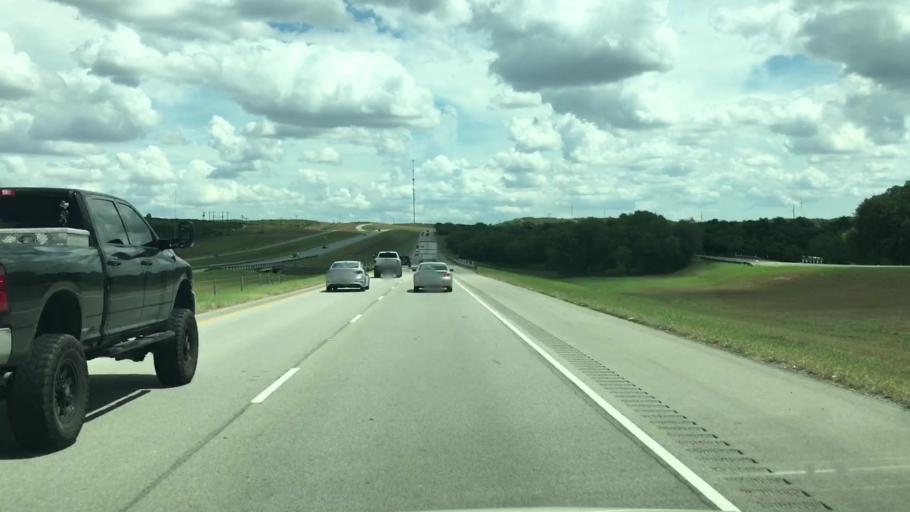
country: US
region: Texas
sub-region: San Patricio County
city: Mathis
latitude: 28.2627
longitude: -97.9322
